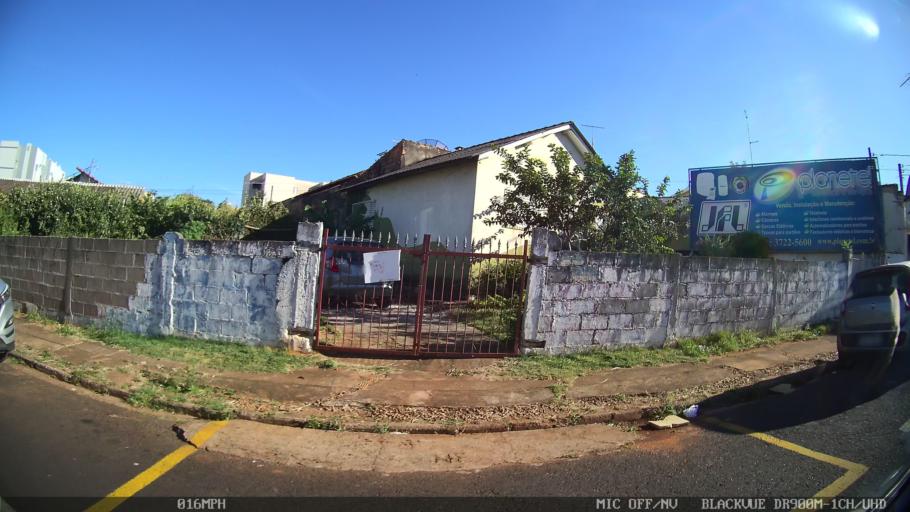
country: BR
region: Sao Paulo
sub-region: Franca
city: Franca
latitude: -20.5508
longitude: -47.4057
